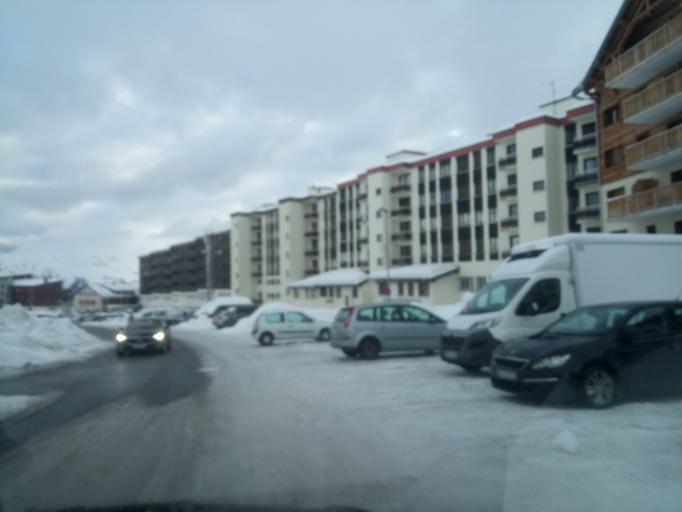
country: FR
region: Rhone-Alpes
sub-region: Departement de la Savoie
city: Saint-Jean-de-Maurienne
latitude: 45.2550
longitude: 6.2589
